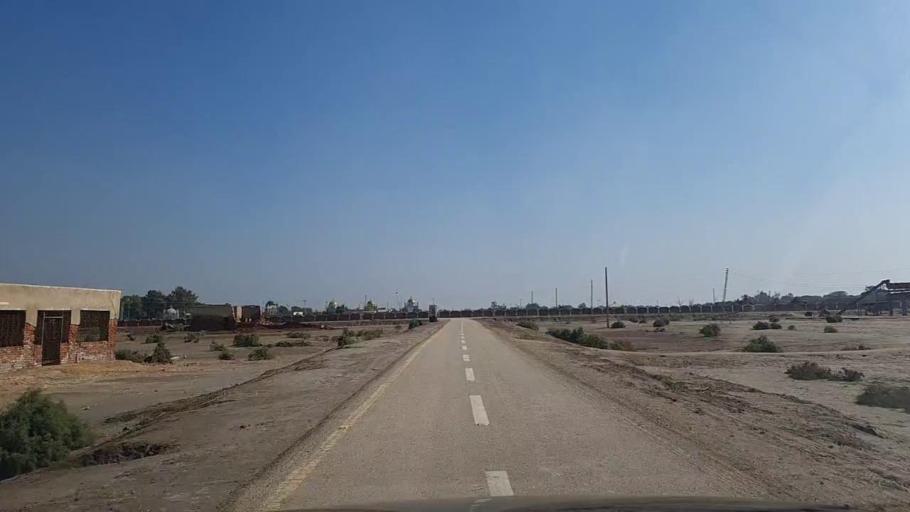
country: PK
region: Sindh
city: Nawabshah
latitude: 26.3200
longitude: 68.3433
